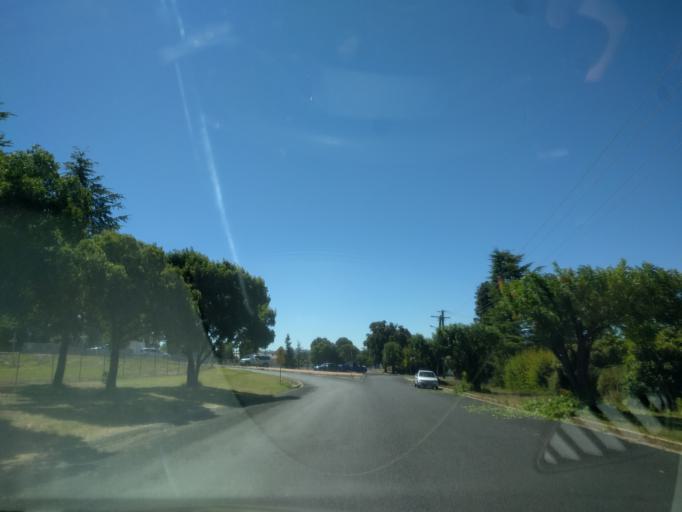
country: AU
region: New South Wales
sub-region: Armidale Dumaresq
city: Armidale
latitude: -30.5200
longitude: 151.6569
